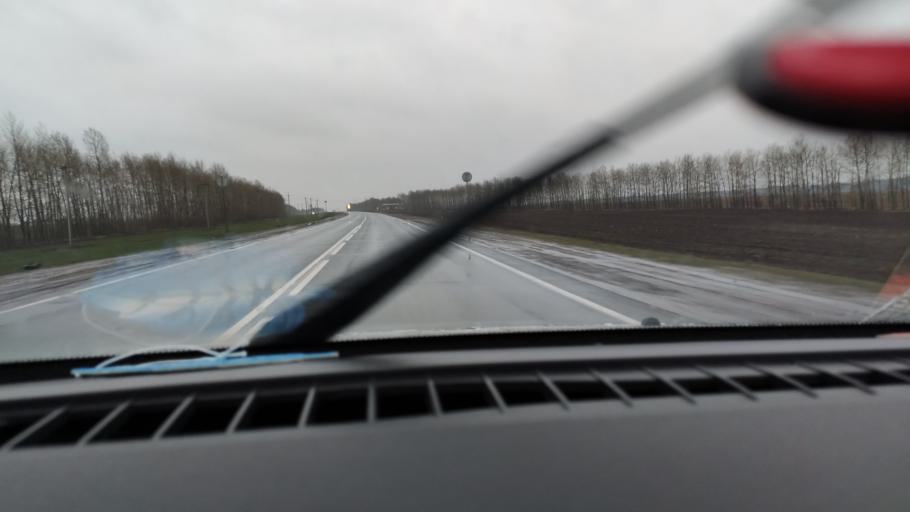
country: RU
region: Tatarstan
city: Mendeleyevsk
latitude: 55.9201
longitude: 52.2742
